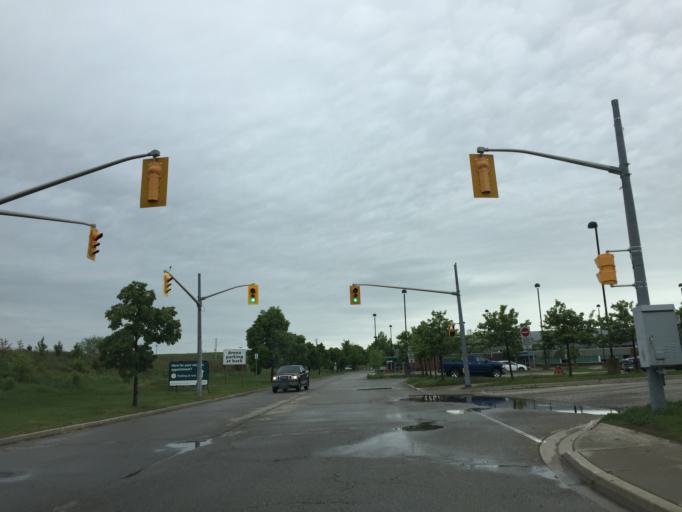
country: CA
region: Ontario
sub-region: Wellington County
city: Guelph
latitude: 43.5247
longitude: -80.2901
